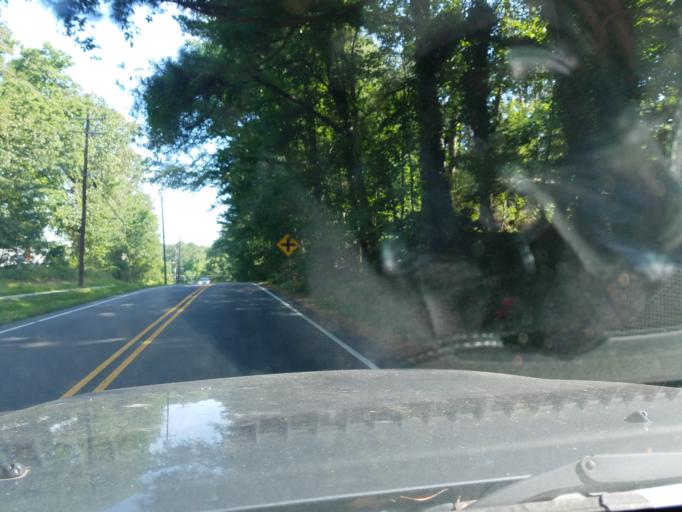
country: US
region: North Carolina
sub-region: Durham County
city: Durham
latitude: 35.9314
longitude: -78.9604
